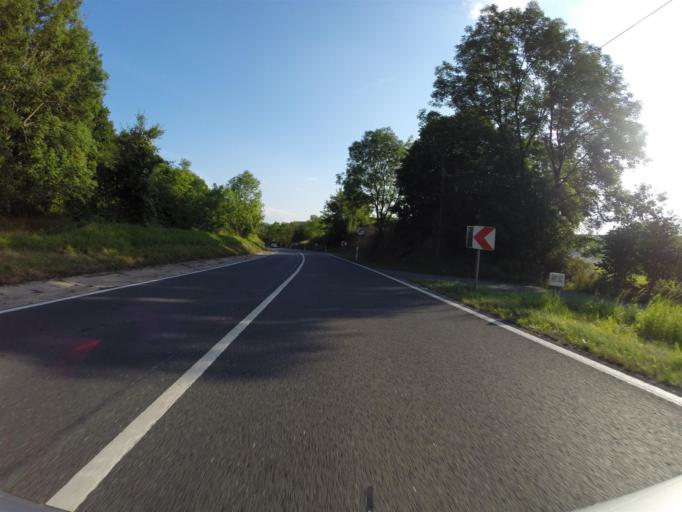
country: DE
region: Thuringia
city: Wichmar
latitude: 51.0296
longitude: 11.6941
